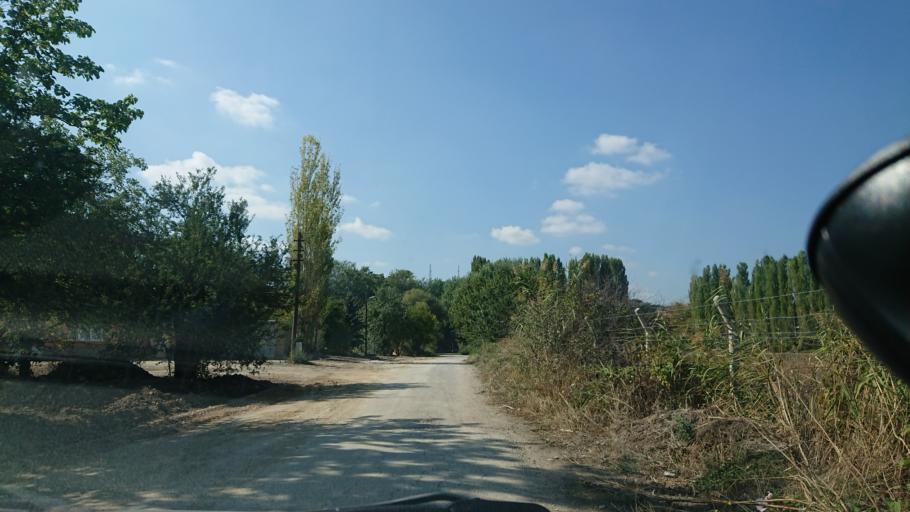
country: TR
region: Eskisehir
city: Eskisehir
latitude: 39.7545
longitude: 30.4759
